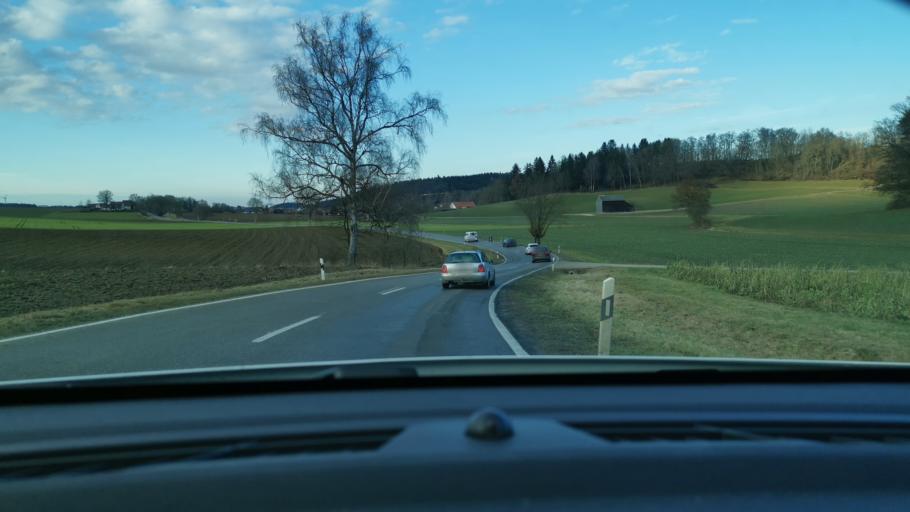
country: DE
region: Bavaria
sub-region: Swabia
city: Petersdorf
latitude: 48.5502
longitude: 10.9962
